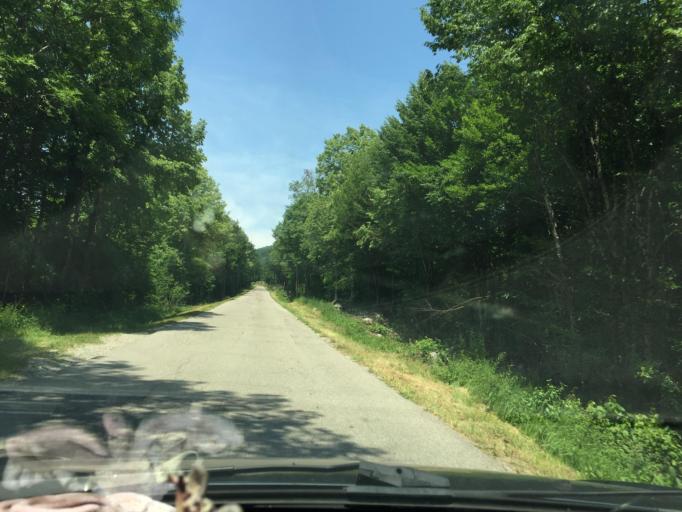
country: HR
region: Istarska
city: Buzet
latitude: 45.4648
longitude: 14.1259
